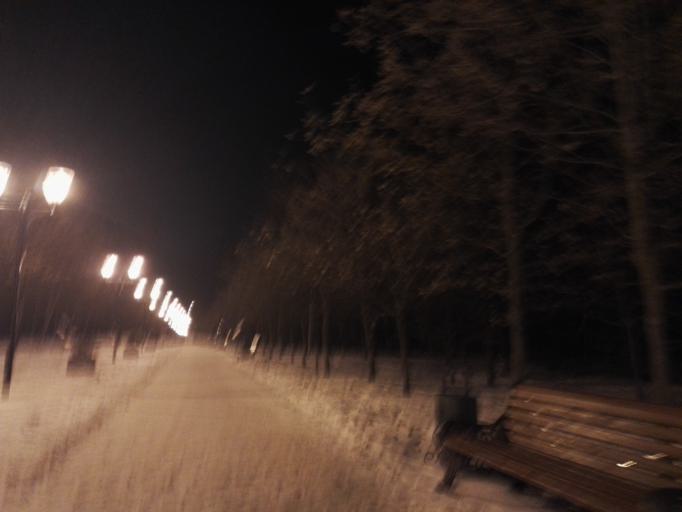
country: RU
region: Tula
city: Tula
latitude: 54.1785
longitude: 37.5881
